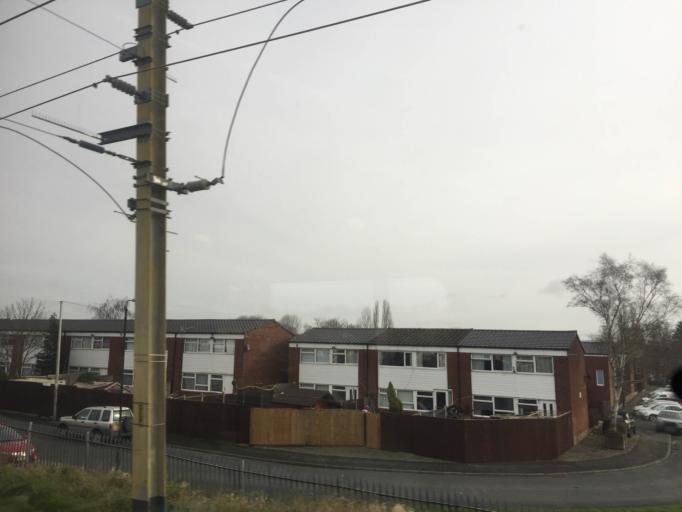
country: GB
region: England
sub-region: Lancashire
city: Coppull
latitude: 53.6262
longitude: -2.6603
